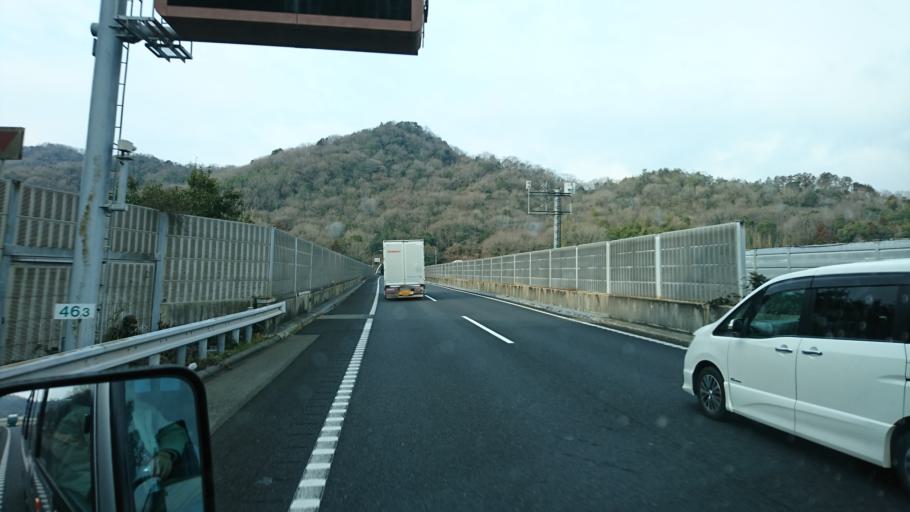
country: JP
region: Hyogo
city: Himeji
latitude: 34.8543
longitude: 134.7779
